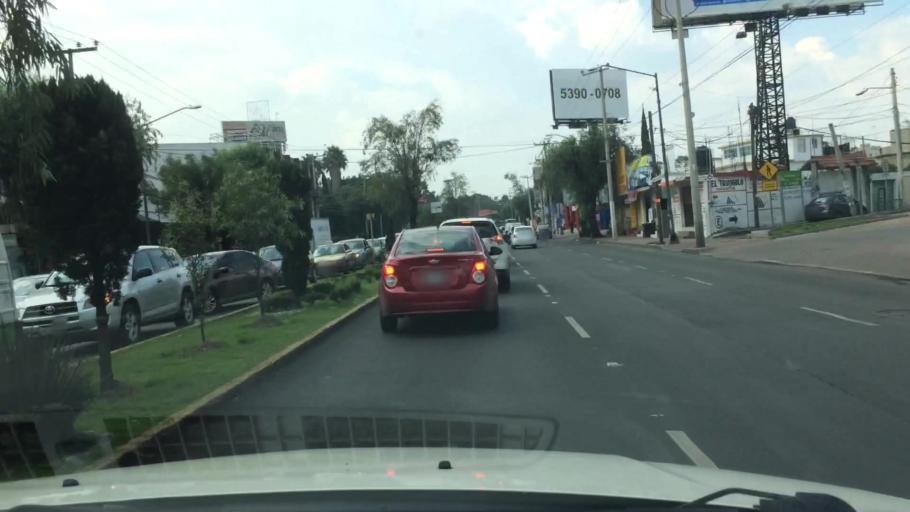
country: MX
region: Mexico City
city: Xochimilco
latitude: 19.2799
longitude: -99.1234
